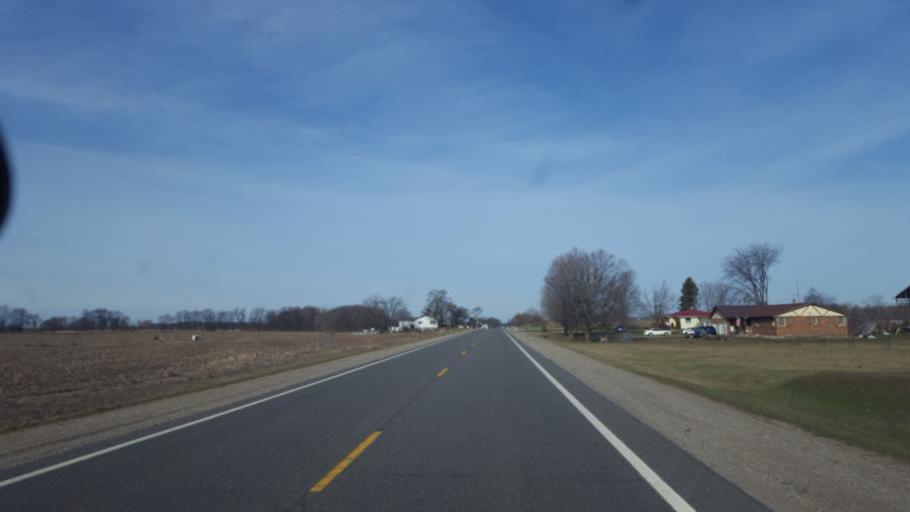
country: US
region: Michigan
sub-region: Montcalm County
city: Lakeview
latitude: 43.4314
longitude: -85.2908
